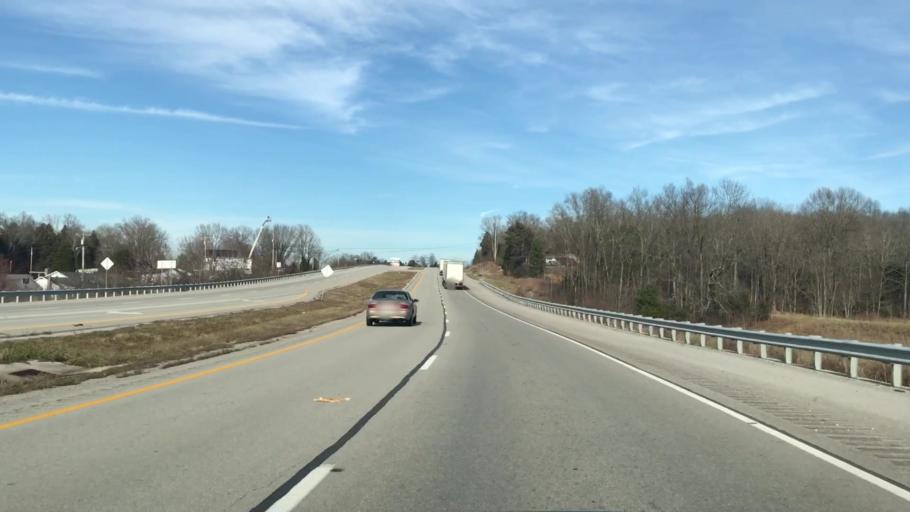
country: US
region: Kentucky
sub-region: Pulaski County
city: Somerset
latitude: 37.0082
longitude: -84.6006
